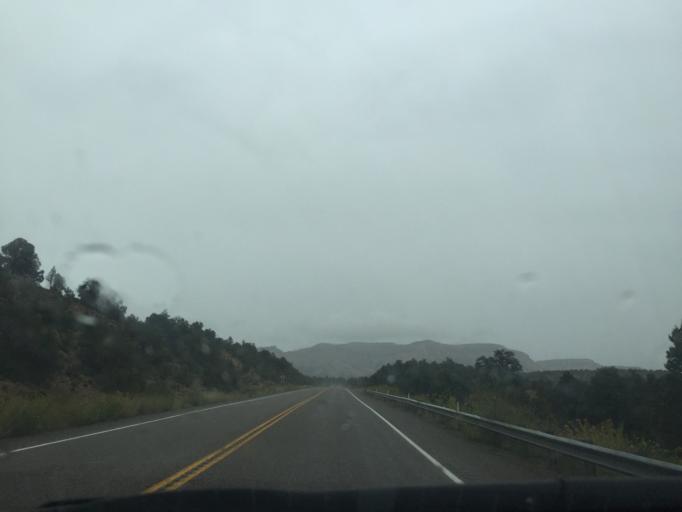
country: US
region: Utah
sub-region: Kane County
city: Kanab
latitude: 37.2035
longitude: -112.6818
